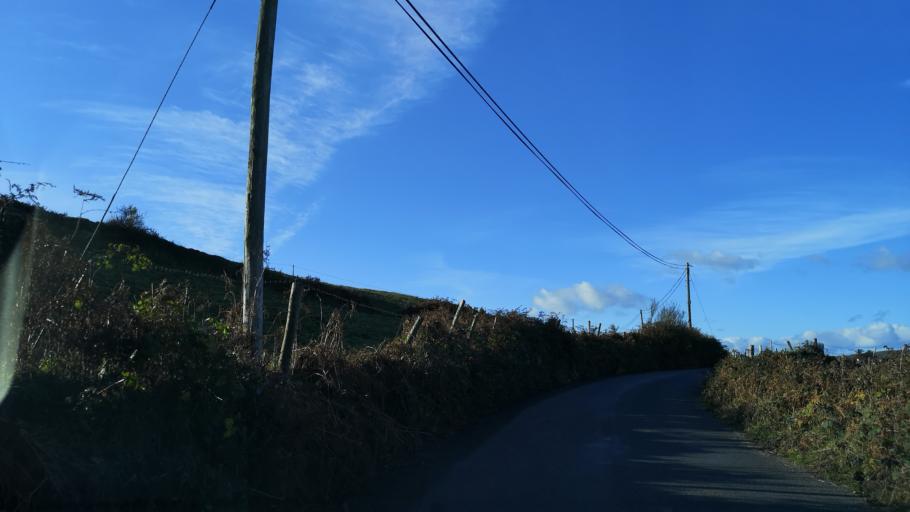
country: IE
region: Connaught
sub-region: County Galway
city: Clifden
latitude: 53.5068
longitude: -10.0883
